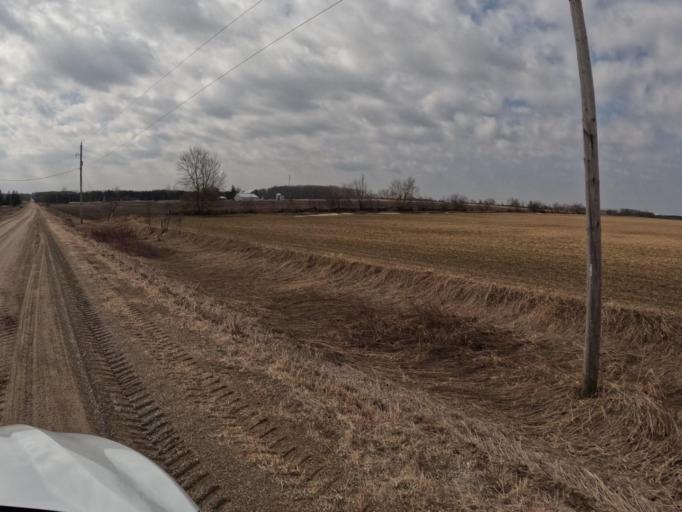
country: CA
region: Ontario
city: Orangeville
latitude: 43.9130
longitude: -80.2379
